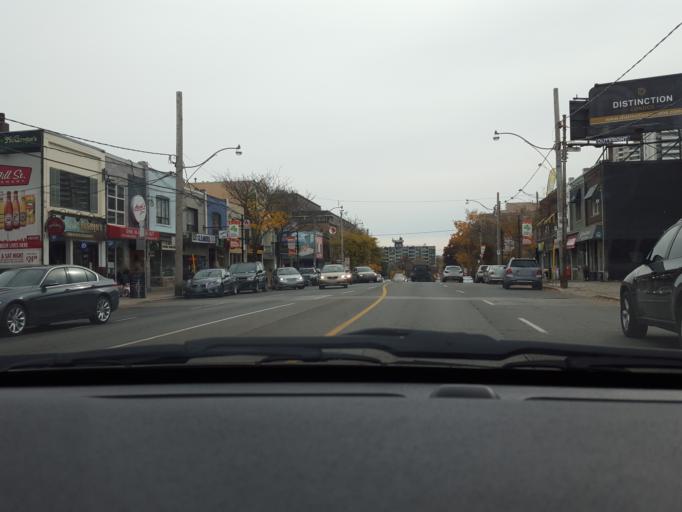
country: CA
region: Ontario
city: Toronto
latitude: 43.7023
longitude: -79.3877
